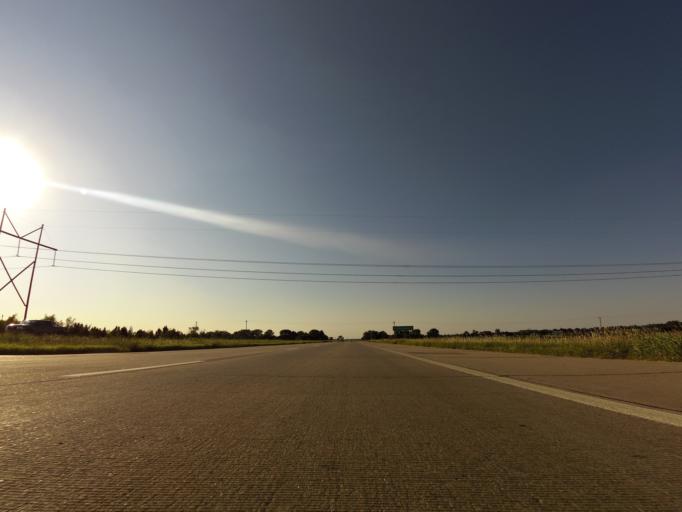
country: US
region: Kansas
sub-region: Sedgwick County
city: Maize
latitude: 37.8073
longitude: -97.4984
